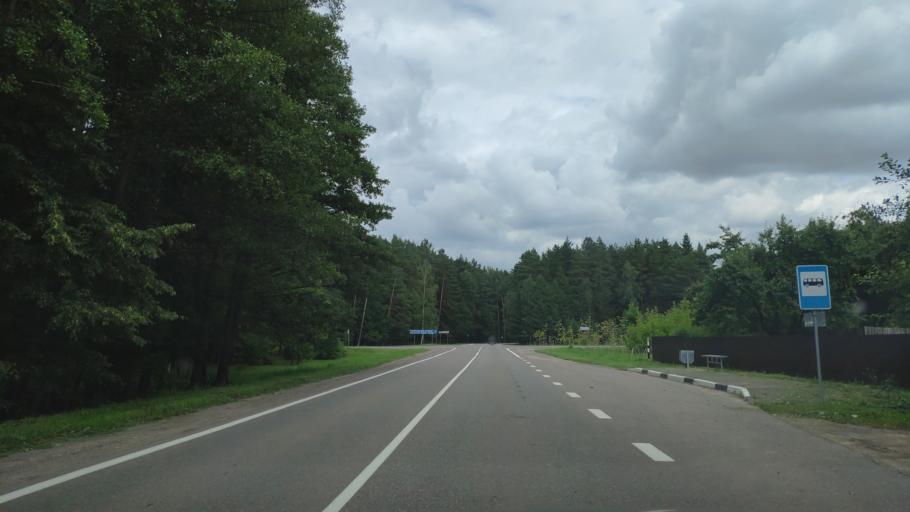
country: BY
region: Minsk
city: Syomkava
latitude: 53.9771
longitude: 27.4419
